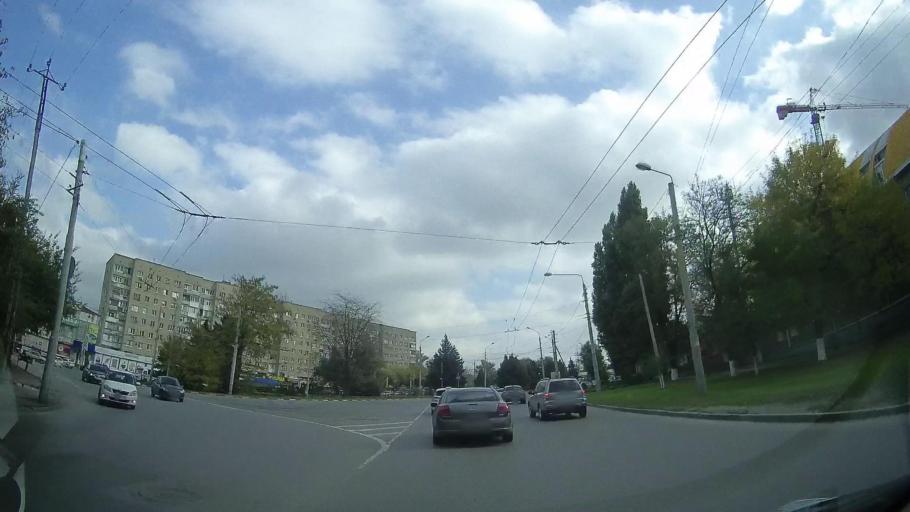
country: RU
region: Rostov
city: Severnyy
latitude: 47.2606
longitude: 39.6880
